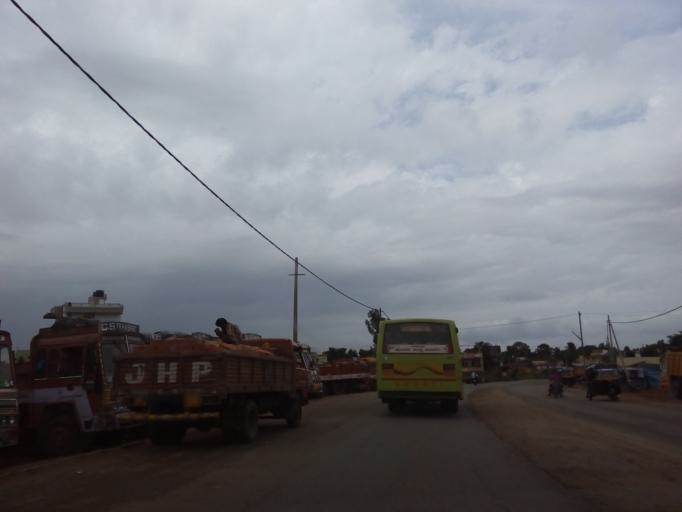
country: IN
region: Karnataka
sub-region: Davanagere
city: Harihar
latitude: 14.5203
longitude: 75.7874
